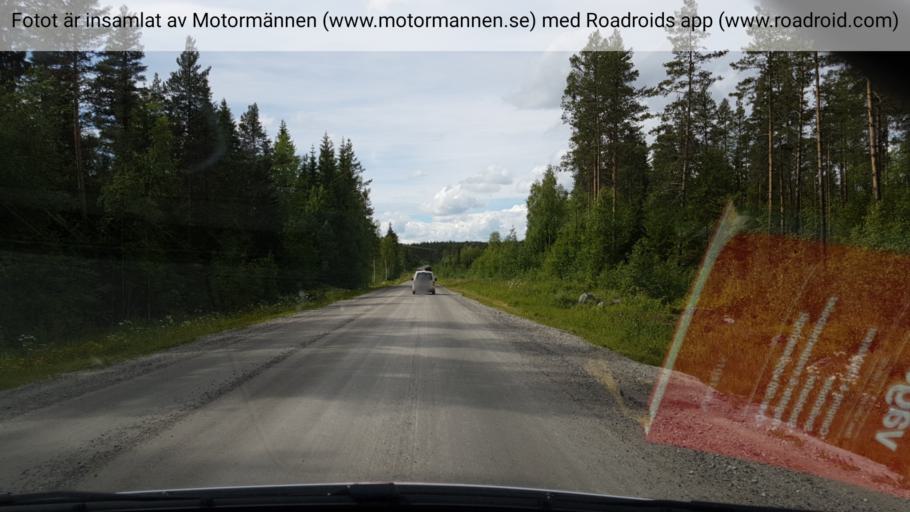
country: SE
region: Vaesternorrland
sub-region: Solleftea Kommun
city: Solleftea
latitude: 63.3120
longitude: 17.2664
